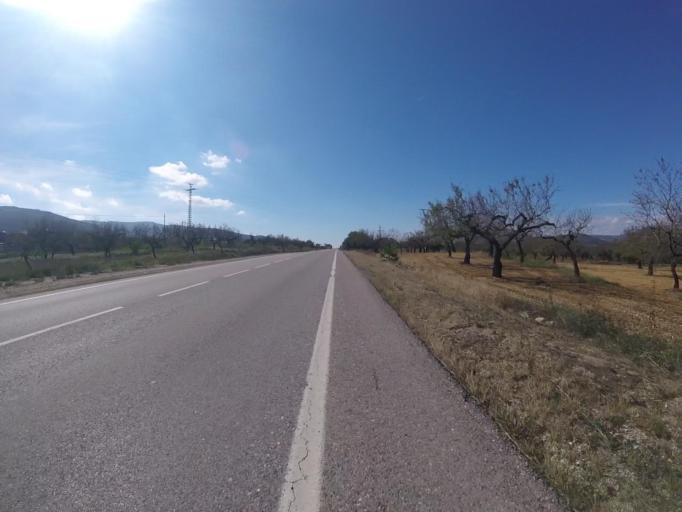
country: ES
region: Valencia
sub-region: Provincia de Castello
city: Albocasser
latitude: 40.3407
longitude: -0.0082
